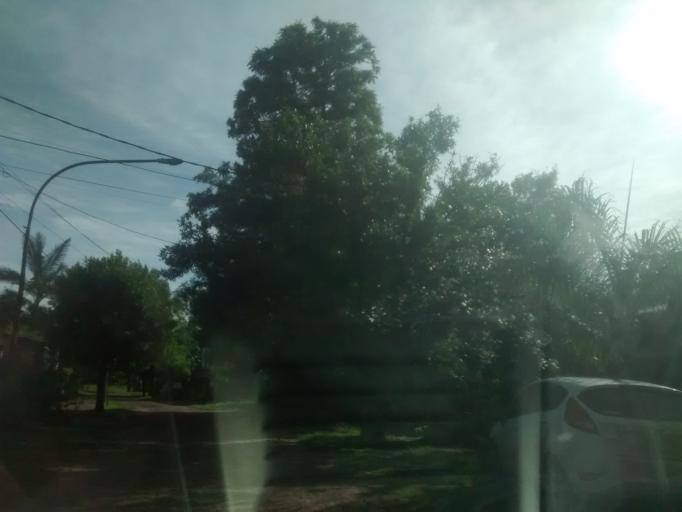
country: AR
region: Chaco
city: Puerto Tirol
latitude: -27.3699
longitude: -59.0872
